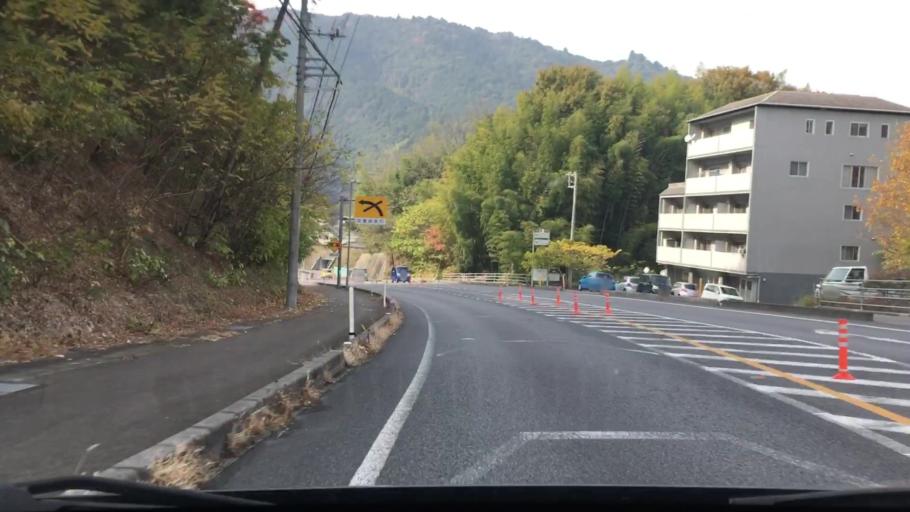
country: JP
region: Yamaguchi
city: Iwakuni
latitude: 34.1574
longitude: 132.1806
